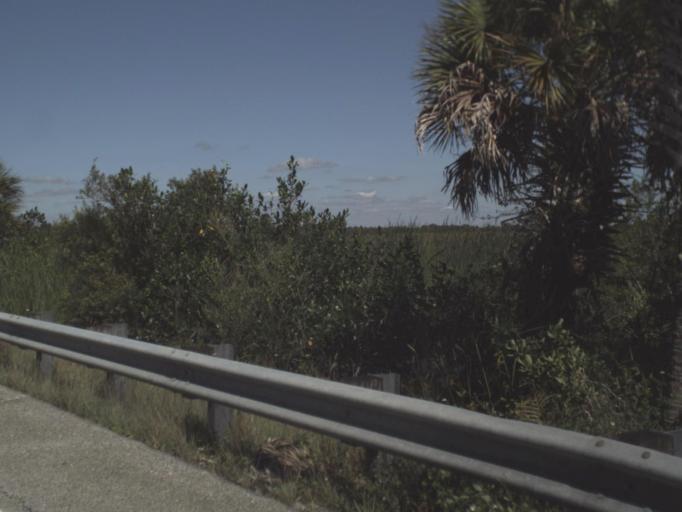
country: US
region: Florida
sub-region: Collier County
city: Marco
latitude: 25.9476
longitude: -81.4788
